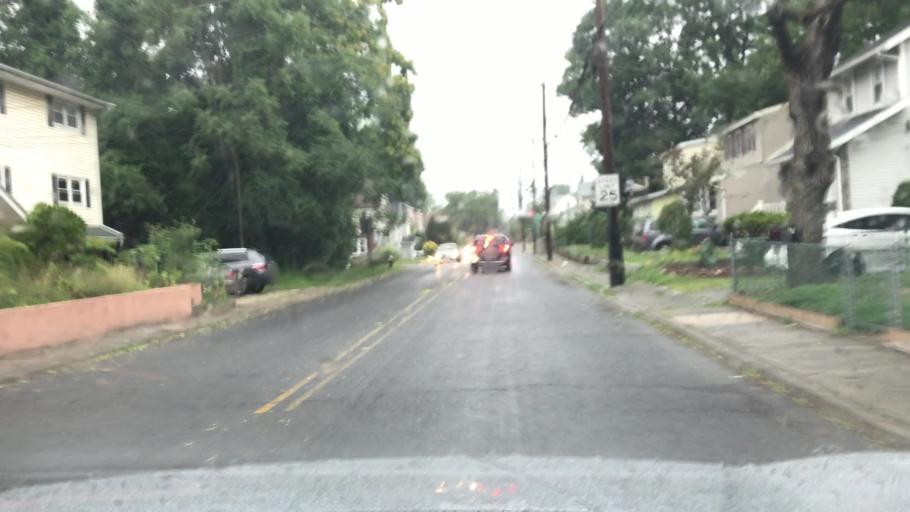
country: US
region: New Jersey
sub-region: Bergen County
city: Dumont
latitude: 40.9364
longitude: -74.0036
